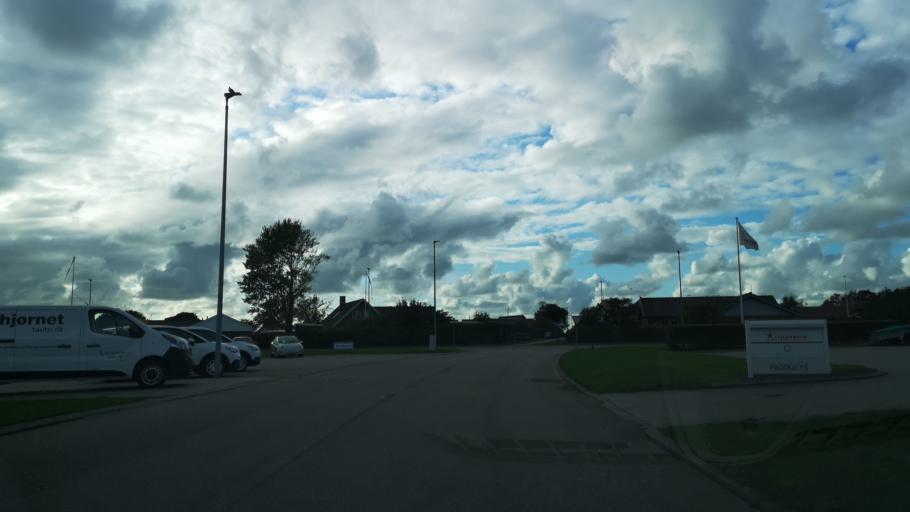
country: DK
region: Central Jutland
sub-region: Ringkobing-Skjern Kommune
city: Ringkobing
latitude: 56.0884
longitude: 8.2671
